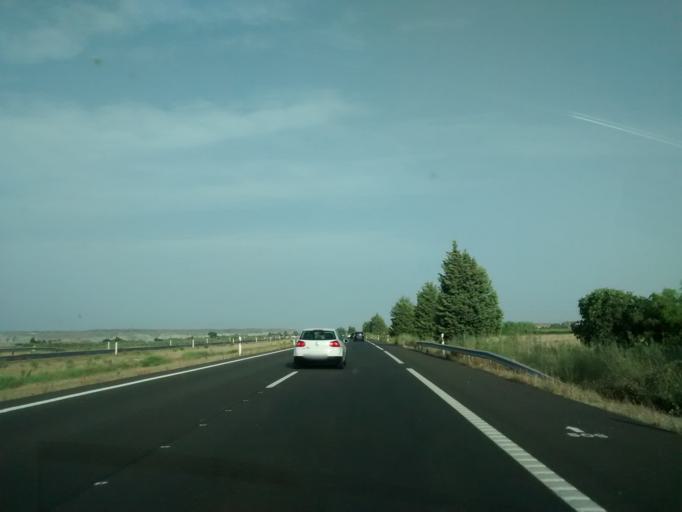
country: ES
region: Aragon
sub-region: Provincia de Zaragoza
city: Utebo
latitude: 41.7222
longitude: -1.0102
